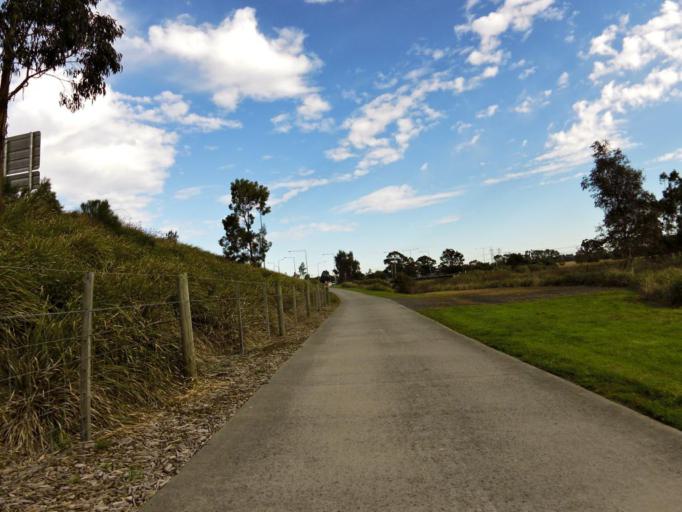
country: AU
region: Victoria
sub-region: Knox
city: Wantirna South
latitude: -37.9017
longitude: 145.2143
